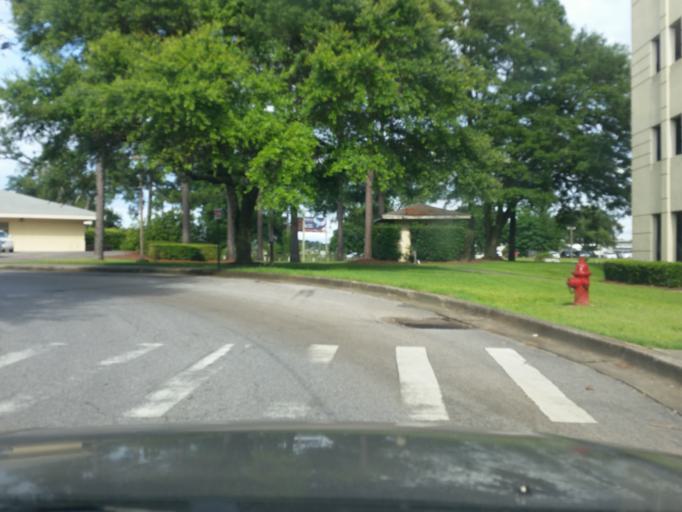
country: US
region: Florida
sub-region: Escambia County
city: Brent
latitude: 30.4783
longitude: -87.2117
